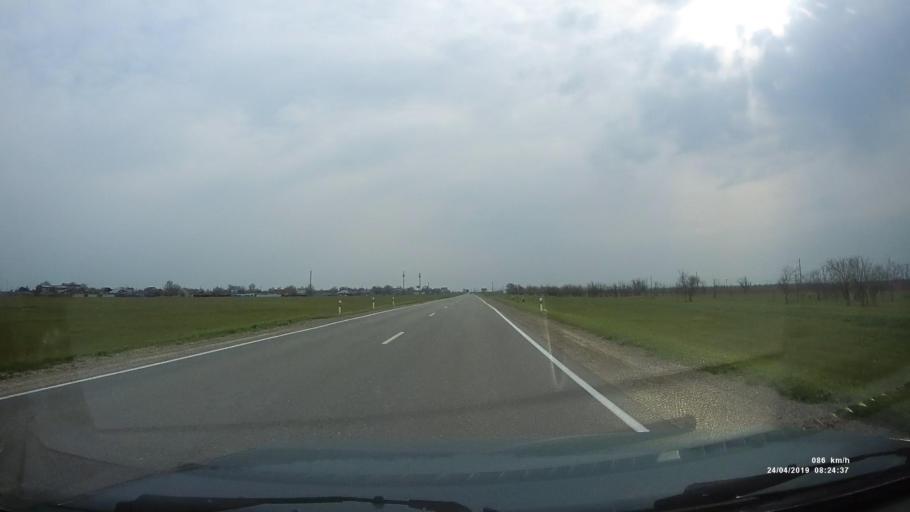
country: RU
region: Kalmykiya
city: Priyutnoye
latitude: 46.1212
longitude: 43.7580
